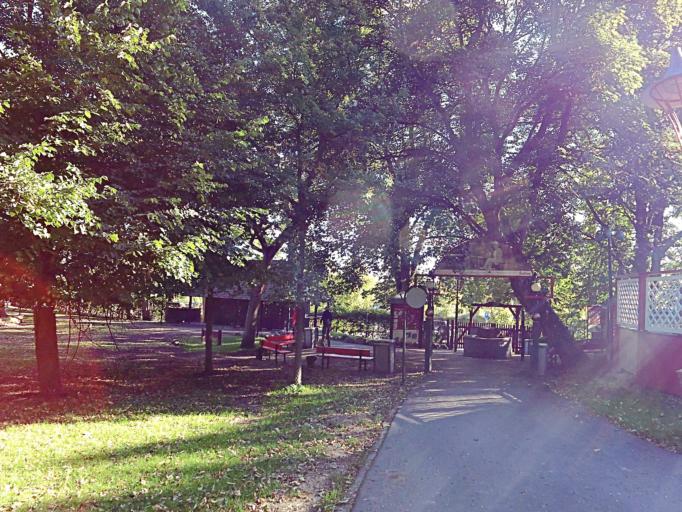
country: DK
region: Capital Region
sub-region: Gentofte Kommune
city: Charlottenlund
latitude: 55.7750
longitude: 12.5774
